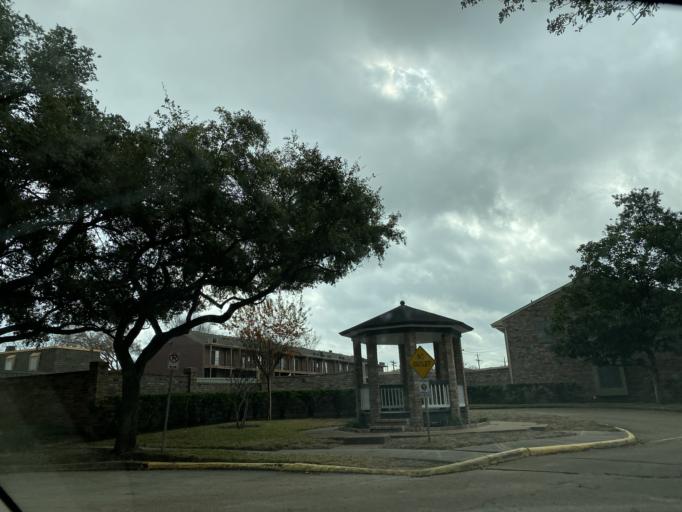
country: US
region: Texas
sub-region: Harris County
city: Piney Point Village
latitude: 29.7424
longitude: -95.4977
